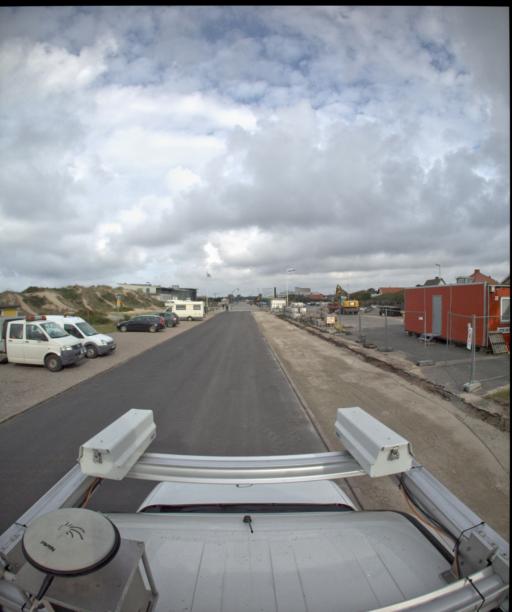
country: SE
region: Halland
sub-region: Falkenbergs Kommun
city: Falkenberg
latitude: 56.8836
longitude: 12.5060
